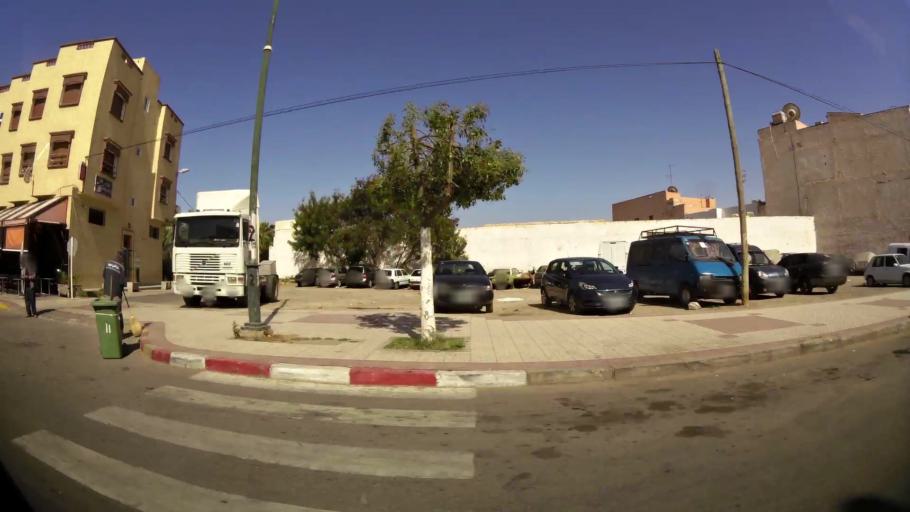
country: MA
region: Souss-Massa-Draa
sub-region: Inezgane-Ait Mellou
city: Inezgane
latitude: 30.3687
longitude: -9.5327
